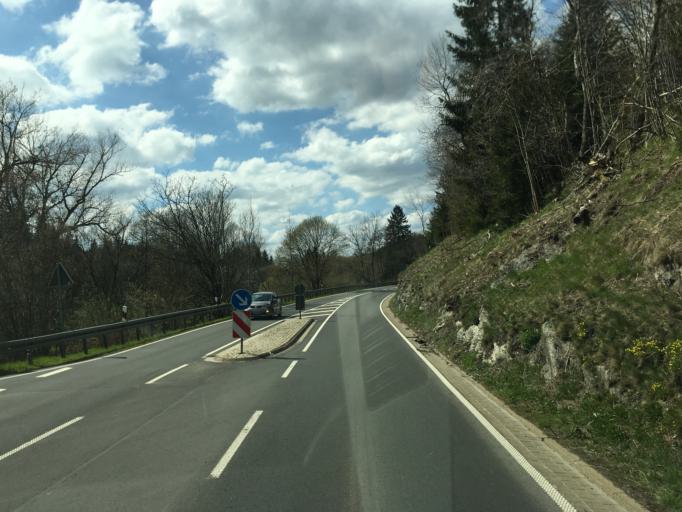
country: DE
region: Saxony-Anhalt
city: Benneckenstein
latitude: 51.6949
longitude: 10.6980
